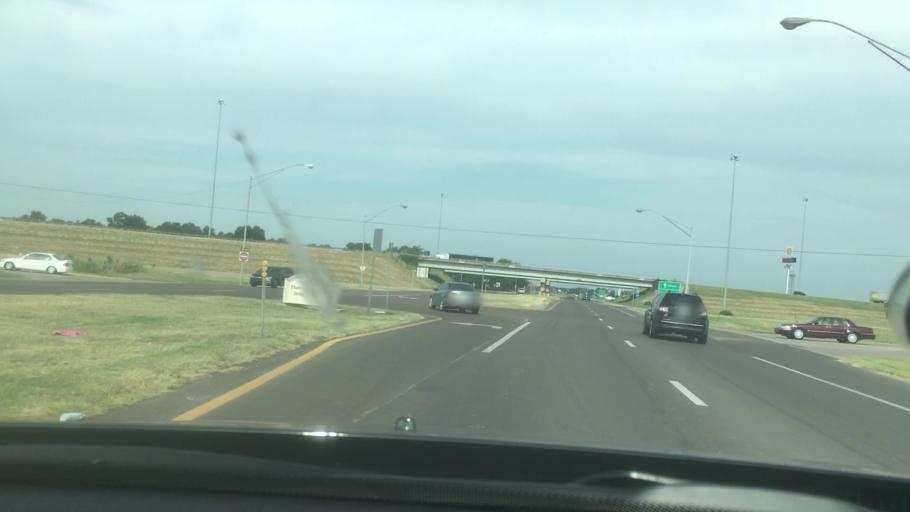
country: US
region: Oklahoma
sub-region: Garvin County
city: Pauls Valley
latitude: 34.7394
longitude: -97.2599
